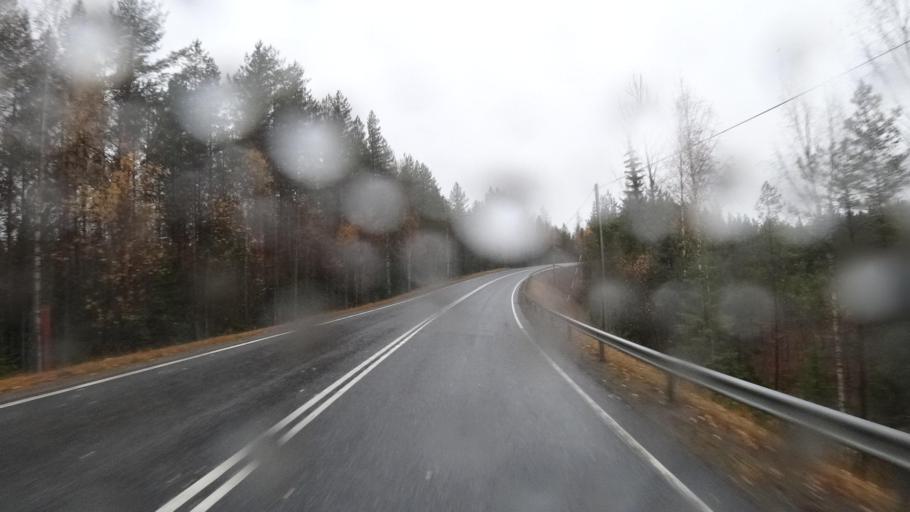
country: FI
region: Northern Savo
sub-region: Koillis-Savo
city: Tuusniemi
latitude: 62.8678
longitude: 28.3992
